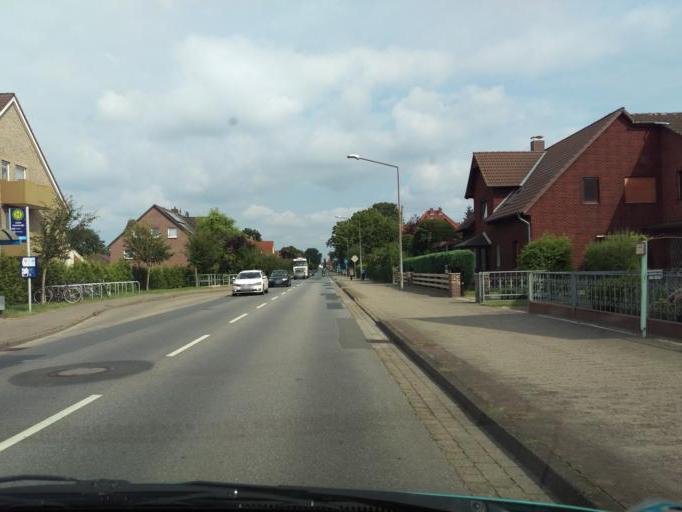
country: DE
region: Lower Saxony
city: Uetze
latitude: 52.4645
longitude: 10.1918
